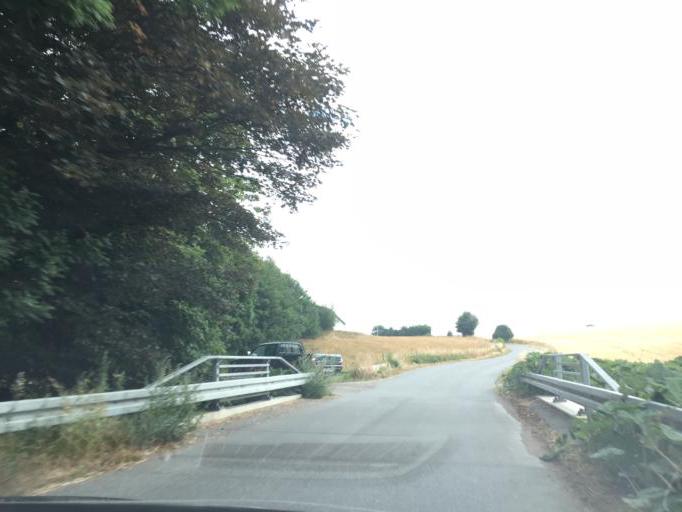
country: DK
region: South Denmark
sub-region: Assens Kommune
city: Assens
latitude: 55.3102
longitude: 9.9693
